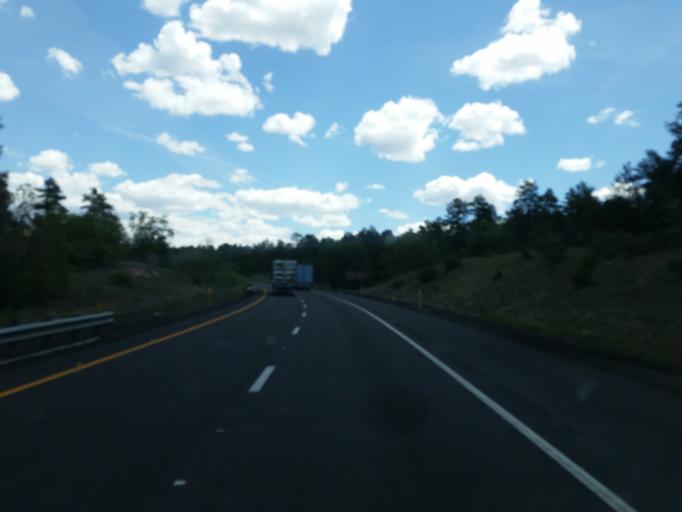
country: US
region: Arizona
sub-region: Coconino County
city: Williams
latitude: 35.2230
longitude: -112.2413
